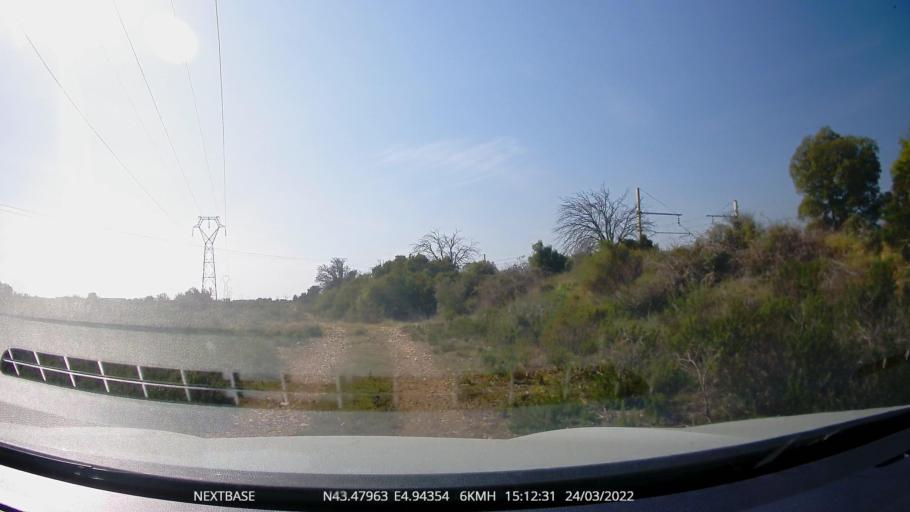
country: FR
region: Provence-Alpes-Cote d'Azur
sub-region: Departement des Bouches-du-Rhone
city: Fos-sur-Mer
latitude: 43.4797
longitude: 4.9431
